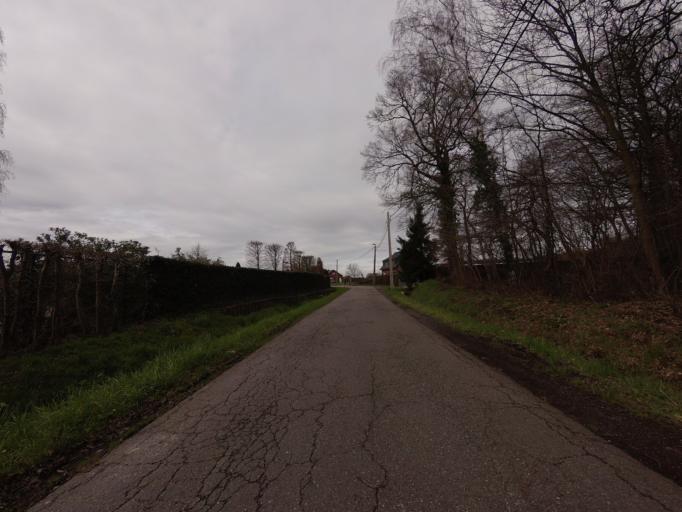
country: BE
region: Flanders
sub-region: Provincie Antwerpen
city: Lint
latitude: 51.1362
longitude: 4.5288
